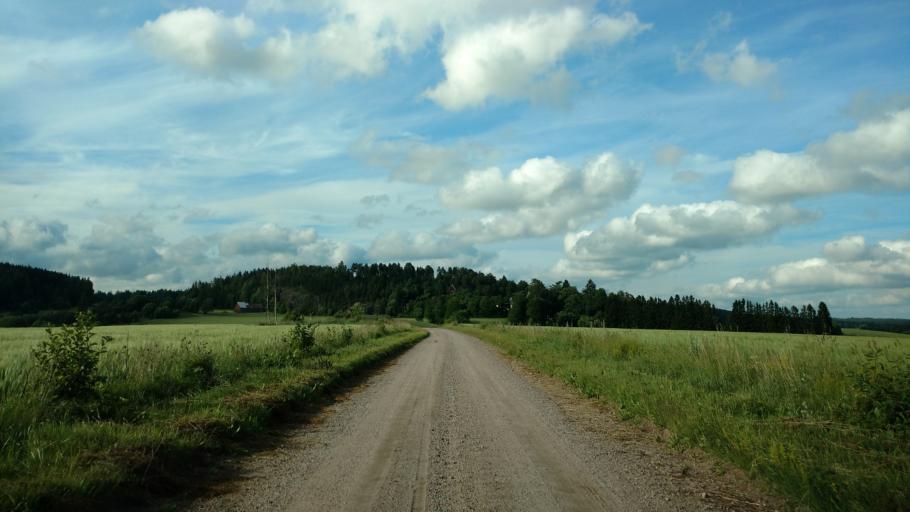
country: FI
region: Varsinais-Suomi
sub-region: Salo
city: Salo
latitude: 60.4208
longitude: 23.1742
